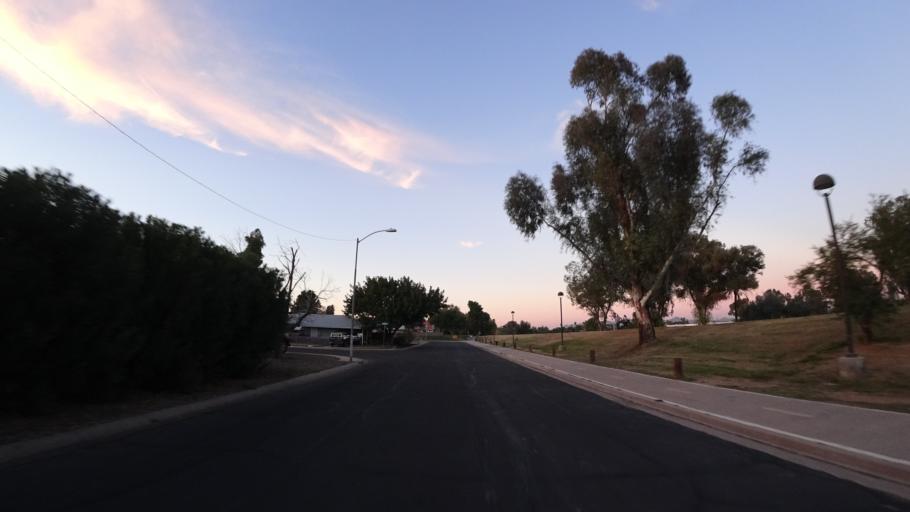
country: US
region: Arizona
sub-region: Maricopa County
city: Scottsdale
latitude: 33.4831
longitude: -111.9131
